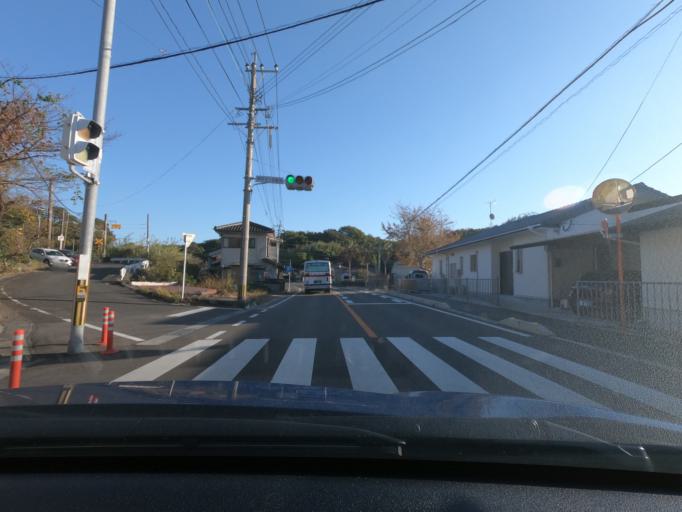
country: JP
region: Kagoshima
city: Akune
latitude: 31.9907
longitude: 130.1981
